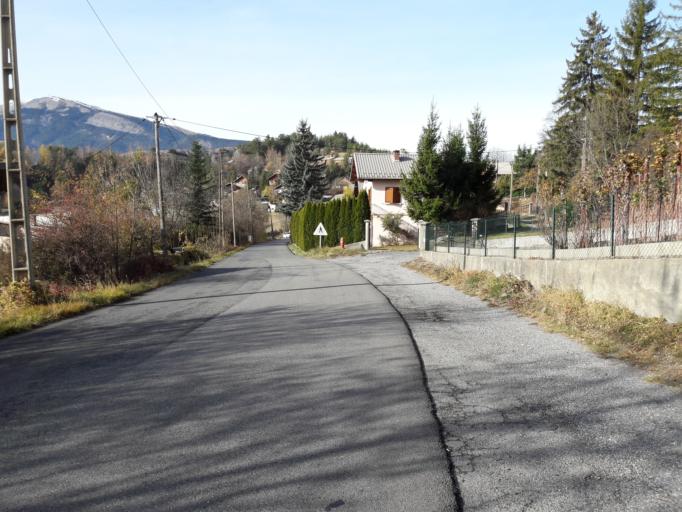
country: FR
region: Provence-Alpes-Cote d'Azur
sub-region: Departement des Alpes-de-Haute-Provence
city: Seyne-les-Alpes
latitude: 44.3545
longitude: 6.3584
